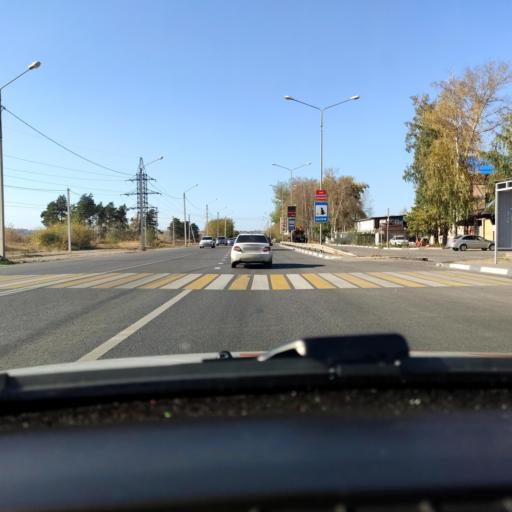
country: RU
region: Voronezj
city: Pridonskoy
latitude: 51.6960
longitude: 39.0878
